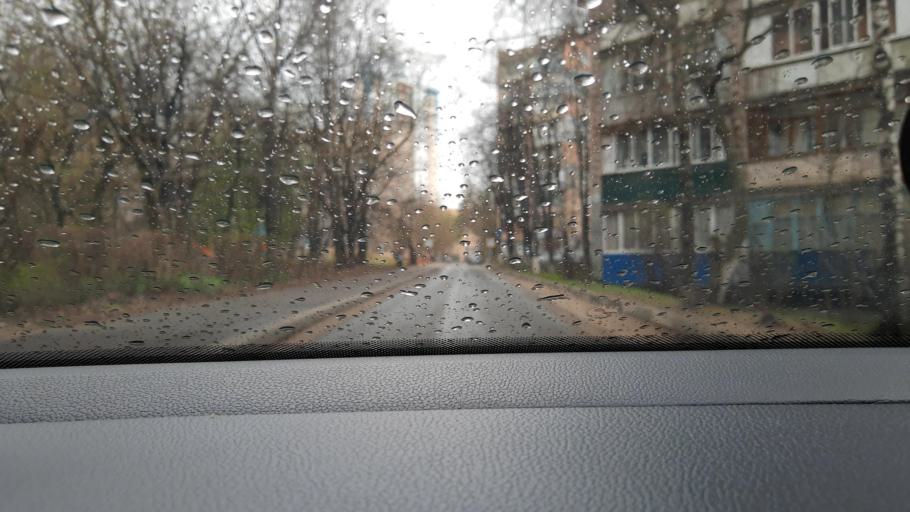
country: RU
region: Moskovskaya
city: Yubileyny
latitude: 55.9362
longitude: 37.8393
